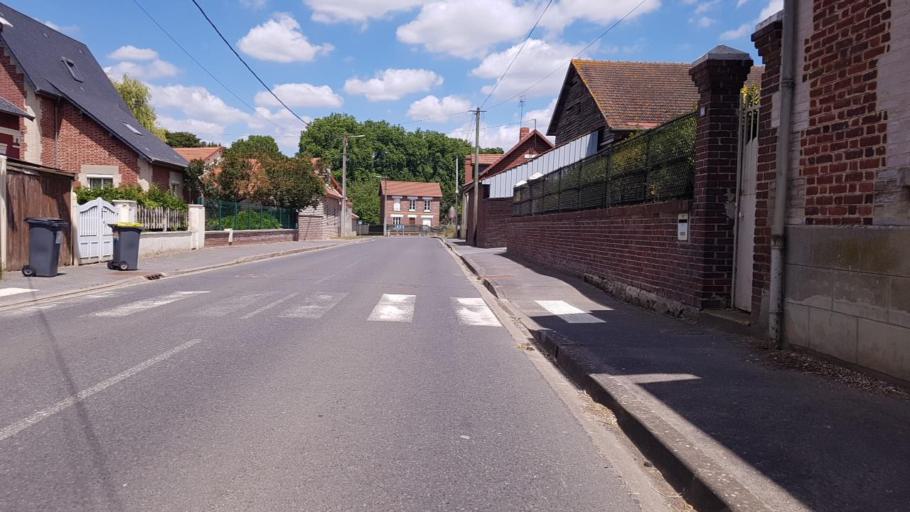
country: FR
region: Picardie
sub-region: Departement de l'Oise
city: Tracy-le-Mont
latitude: 49.5030
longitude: 2.9798
